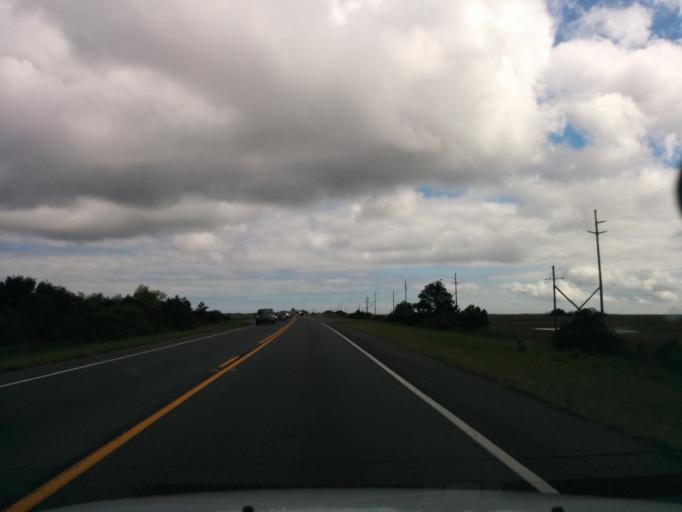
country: US
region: Georgia
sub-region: Glynn County
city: Brunswick
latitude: 31.0915
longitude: -81.4820
